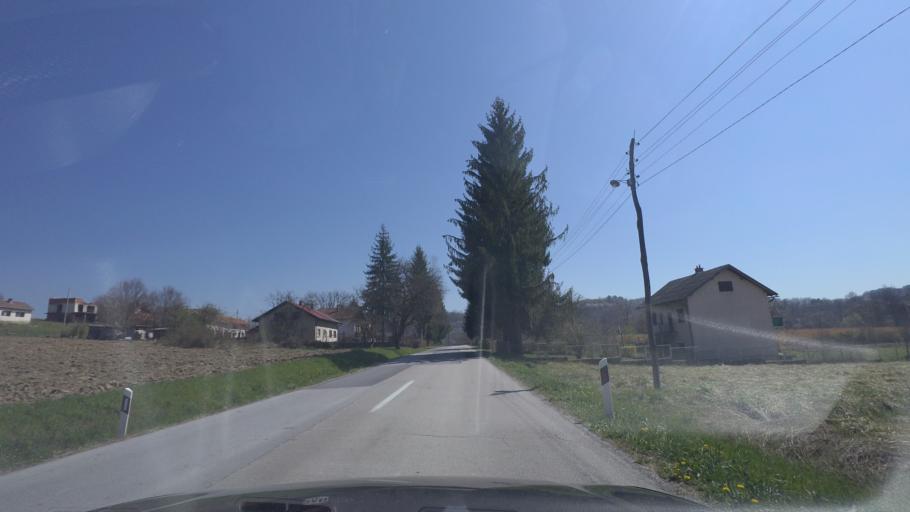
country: HR
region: Karlovacka
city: Vojnic
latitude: 45.3765
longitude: 15.6143
